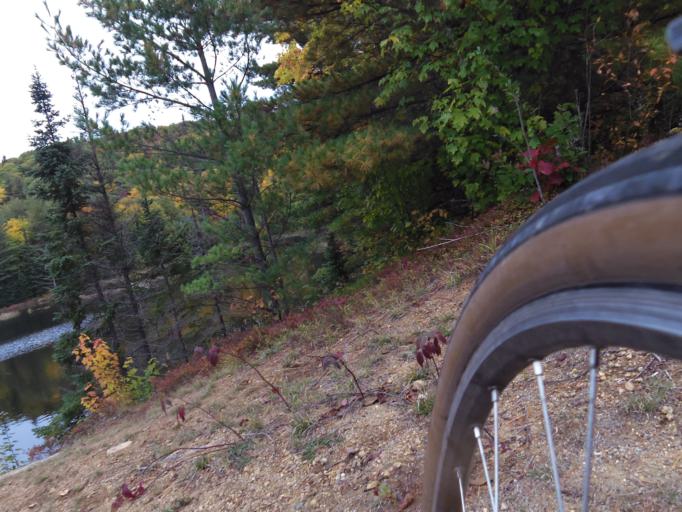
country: CA
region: Quebec
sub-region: Outaouais
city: Wakefield
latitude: 45.6001
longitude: -76.0669
